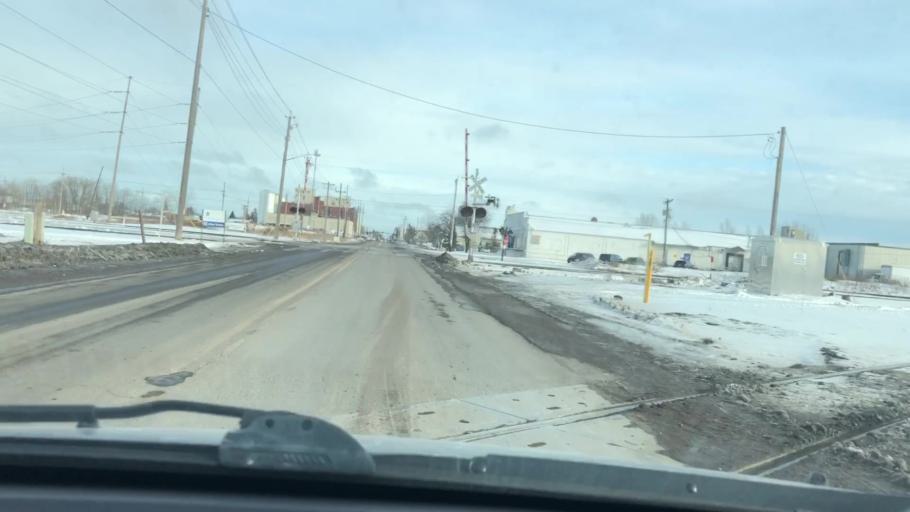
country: US
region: Wisconsin
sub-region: Douglas County
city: Superior
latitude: 46.7279
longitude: -92.1119
